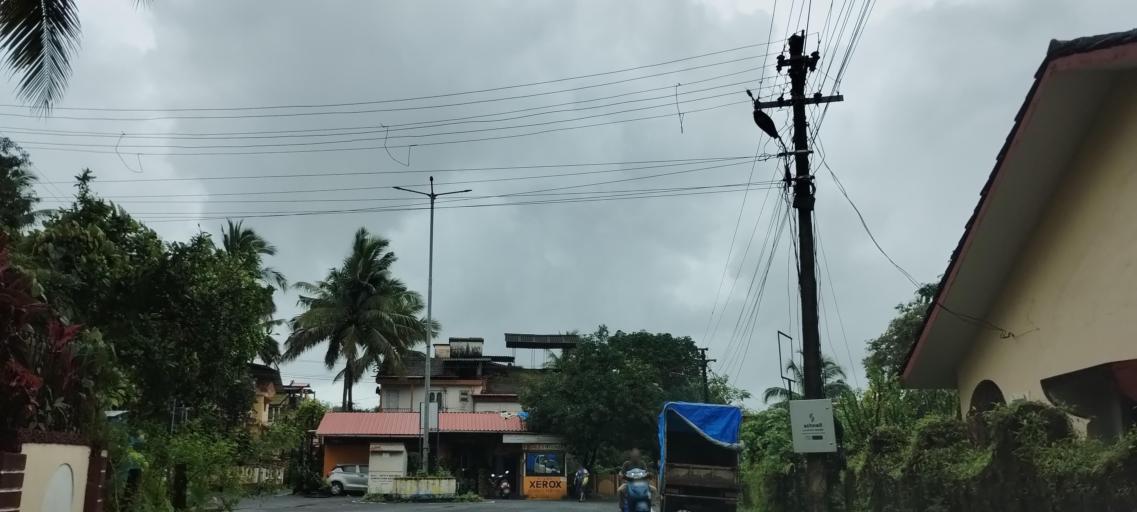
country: IN
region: Goa
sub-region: North Goa
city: Aldona
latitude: 15.5878
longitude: 73.8686
